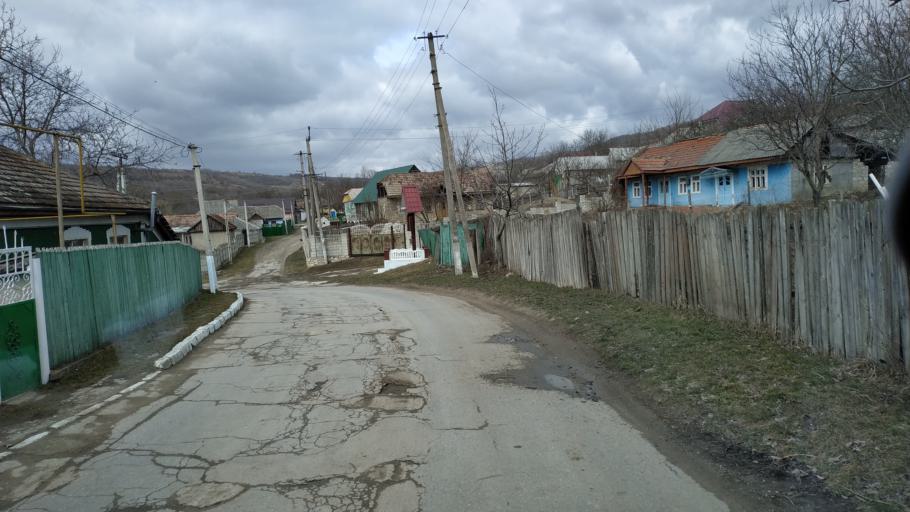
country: MD
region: Stinga Nistrului
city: Bucovat
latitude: 47.2326
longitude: 28.4450
